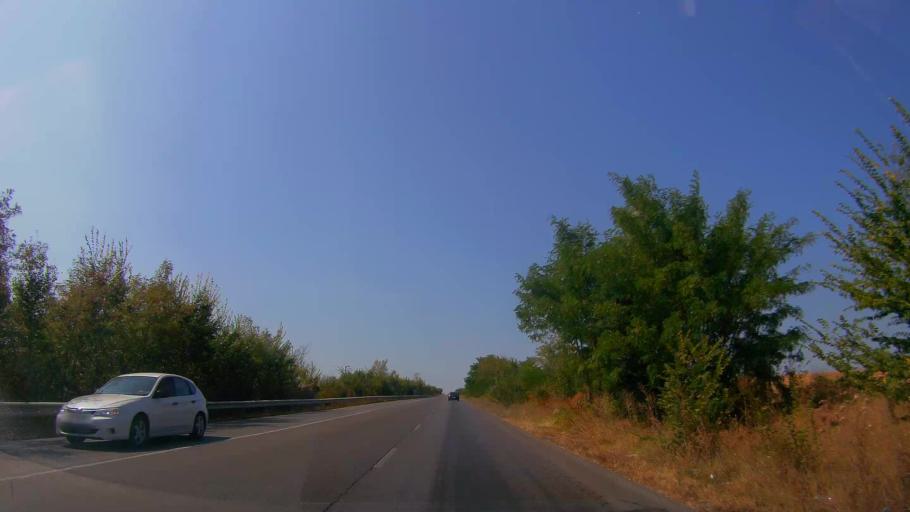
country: BG
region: Ruse
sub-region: Obshtina Vetovo
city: Senovo
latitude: 43.5609
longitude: 26.3697
